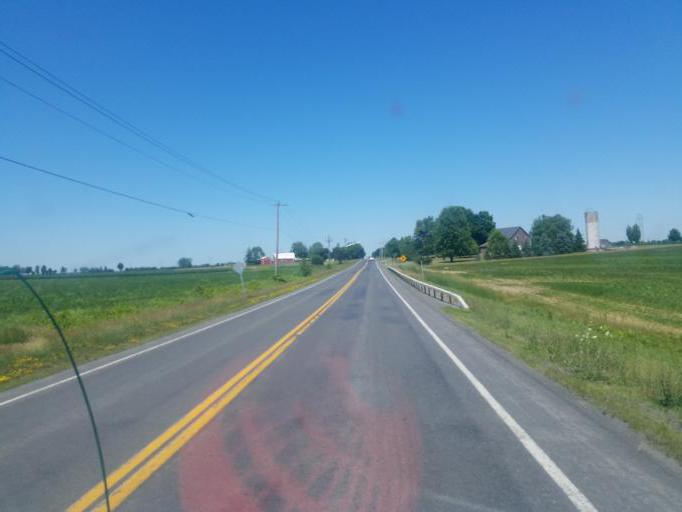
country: US
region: New York
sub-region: Ontario County
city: Geneva
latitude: 42.7657
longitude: -77.0133
